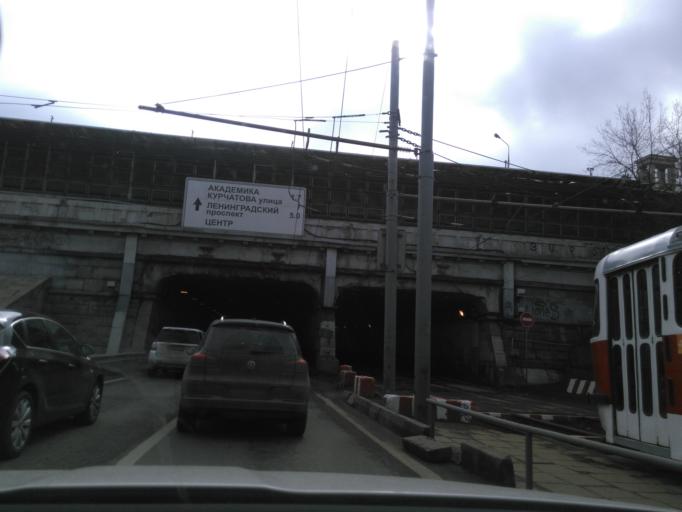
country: RU
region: Moscow
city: Pokrovskoye-Streshnevo
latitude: 55.8194
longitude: 37.4510
